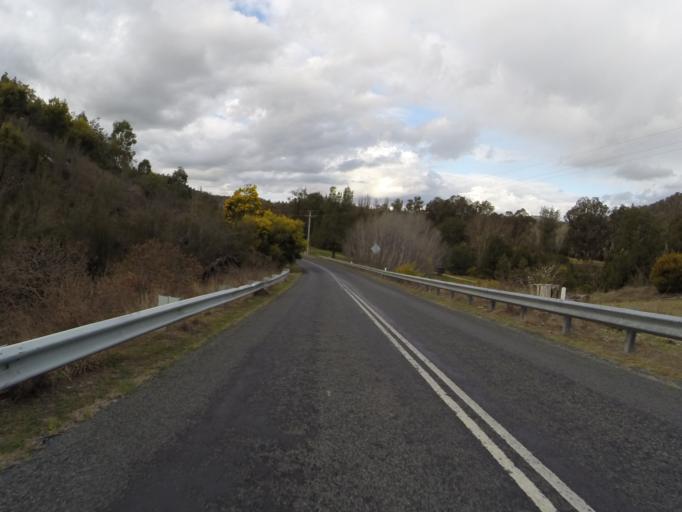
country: AU
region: Australian Capital Territory
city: Macquarie
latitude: -35.3276
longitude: 148.9363
